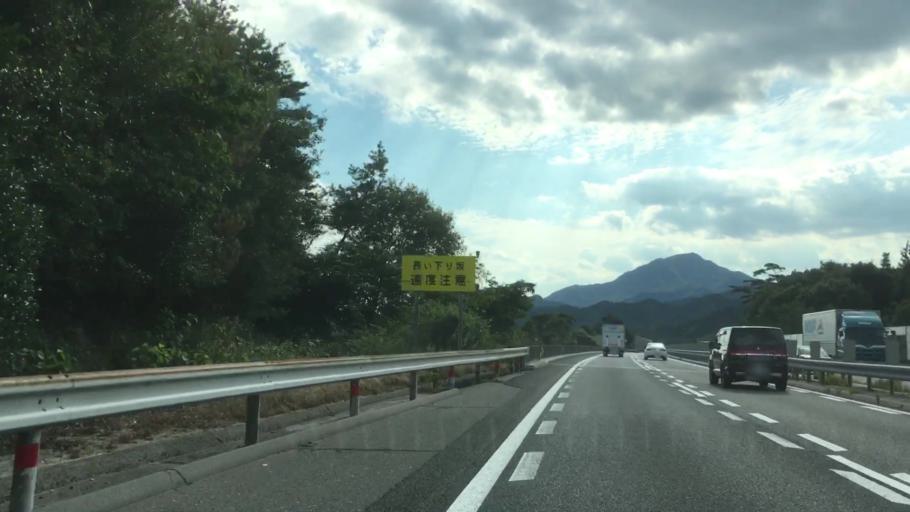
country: JP
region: Hiroshima
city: Miyajima
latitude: 34.3251
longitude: 132.2906
